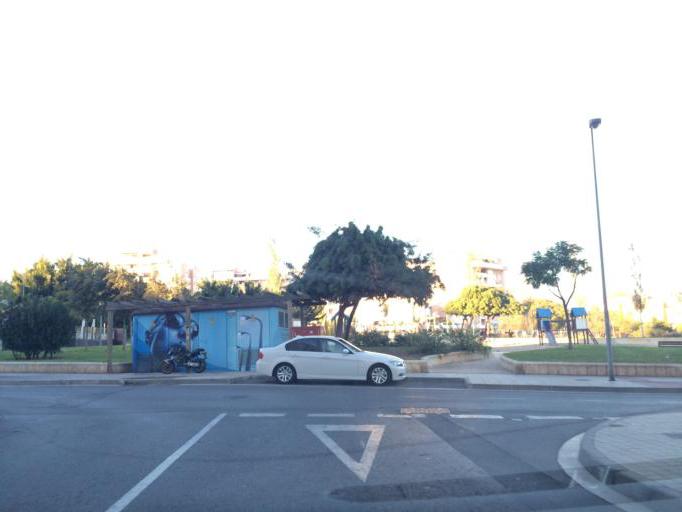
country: ES
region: Andalusia
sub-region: Provincia de Almeria
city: Almeria
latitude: 36.8557
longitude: -2.4449
